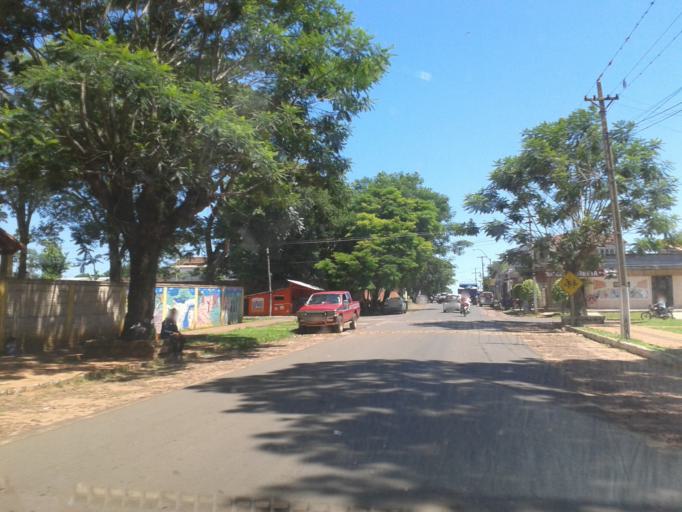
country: PY
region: Misiones
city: Santa Rosa
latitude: -26.8886
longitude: -56.8482
